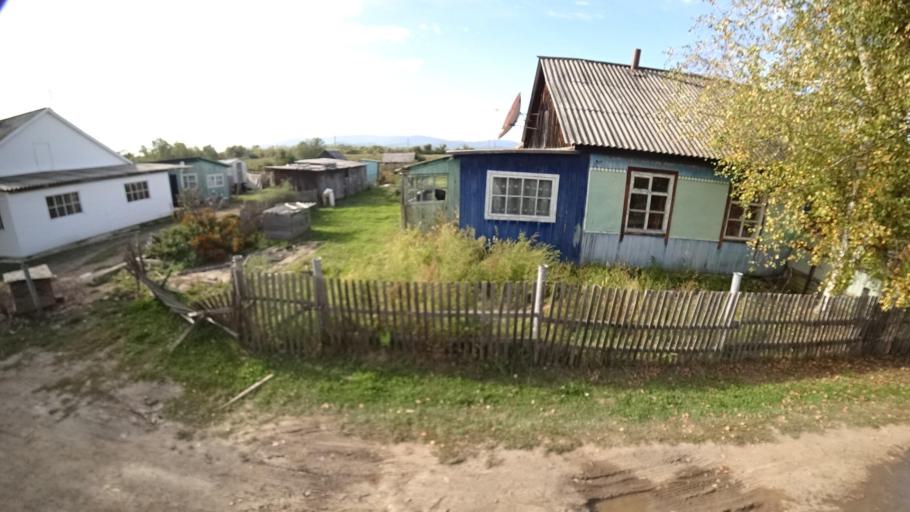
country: RU
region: Primorskiy
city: Dostoyevka
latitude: 44.3070
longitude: 133.4623
